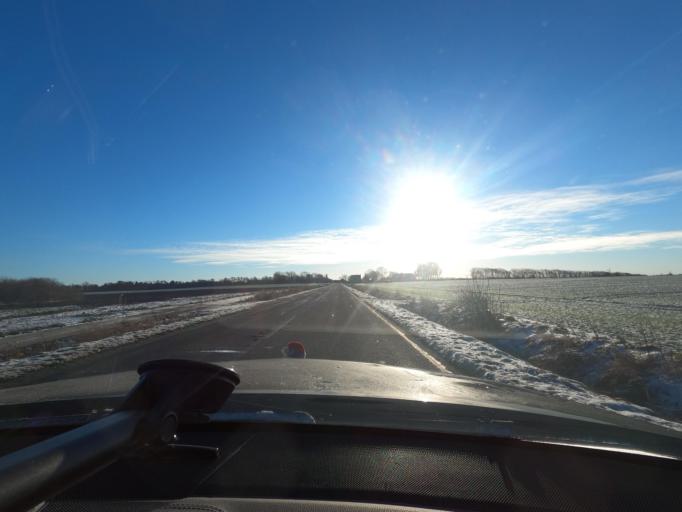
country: DK
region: South Denmark
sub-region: Sonderborg Kommune
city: Horuphav
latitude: 54.8712
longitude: 9.9959
